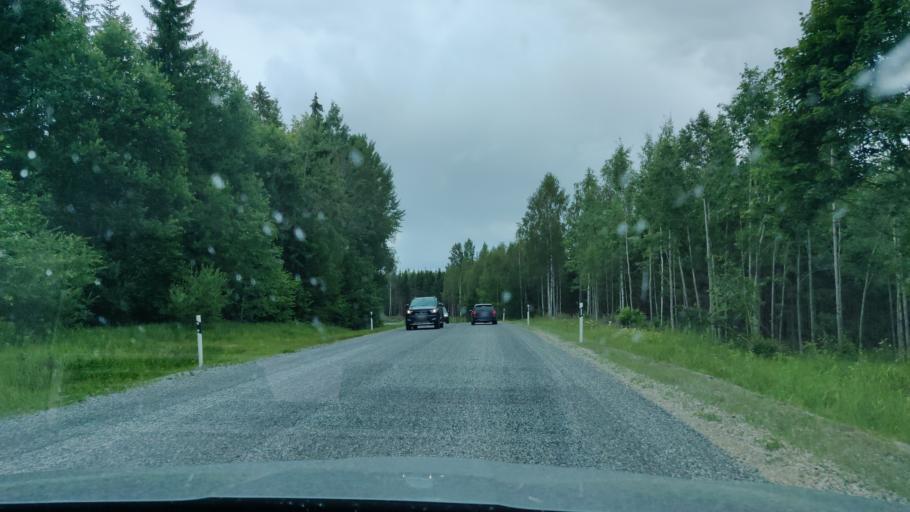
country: EE
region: Vorumaa
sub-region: Antsla vald
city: Vana-Antsla
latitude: 58.0272
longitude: 26.5773
